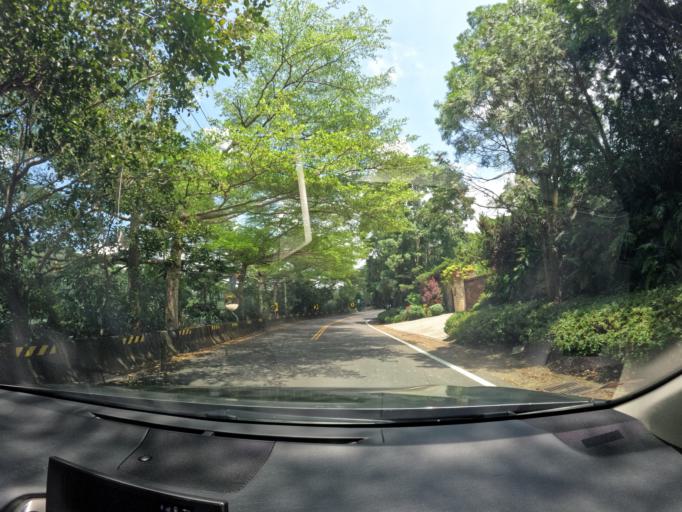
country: TW
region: Taiwan
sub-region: Miaoli
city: Miaoli
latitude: 24.4086
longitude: 120.7863
